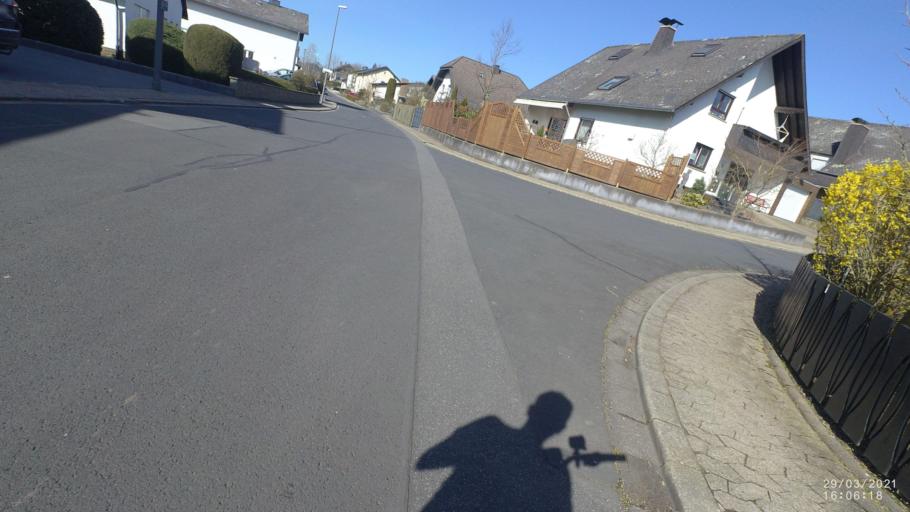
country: DE
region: Rheinland-Pfalz
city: Plaidt
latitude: 50.3893
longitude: 7.3984
